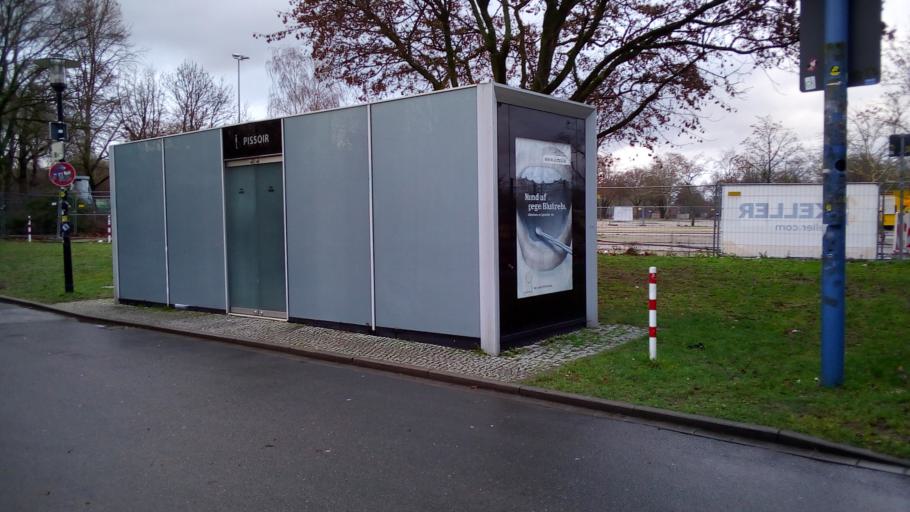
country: DE
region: North Rhine-Westphalia
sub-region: Regierungsbezirk Arnsberg
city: Dortmund
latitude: 51.4917
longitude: 7.4565
